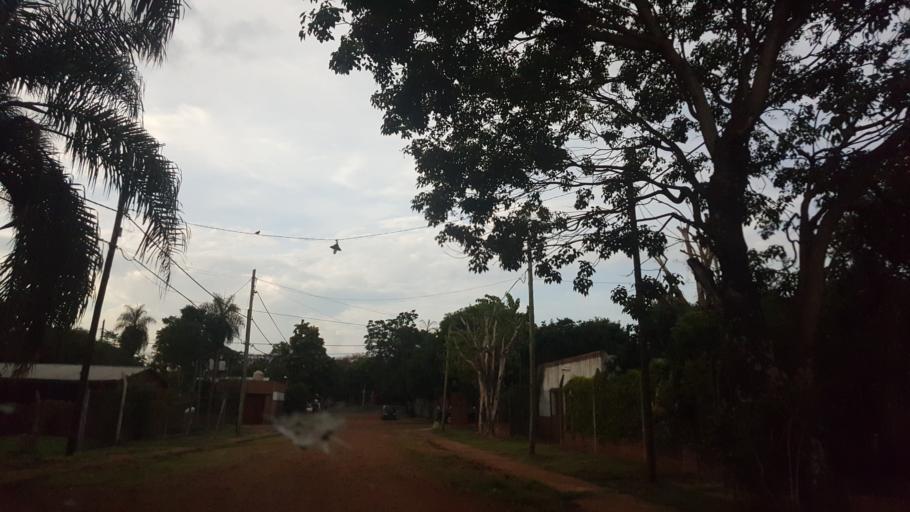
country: AR
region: Misiones
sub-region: Departamento de Capital
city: Posadas
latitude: -27.3905
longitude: -55.9169
